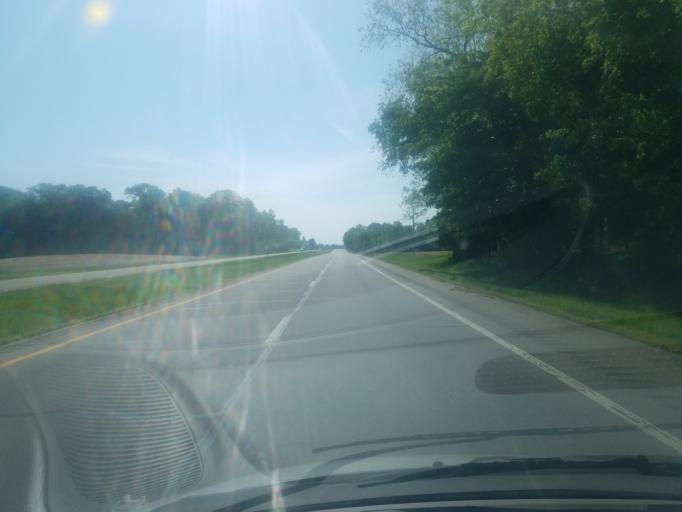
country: US
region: Ohio
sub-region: Huron County
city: Bellevue
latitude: 41.2625
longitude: -82.7724
